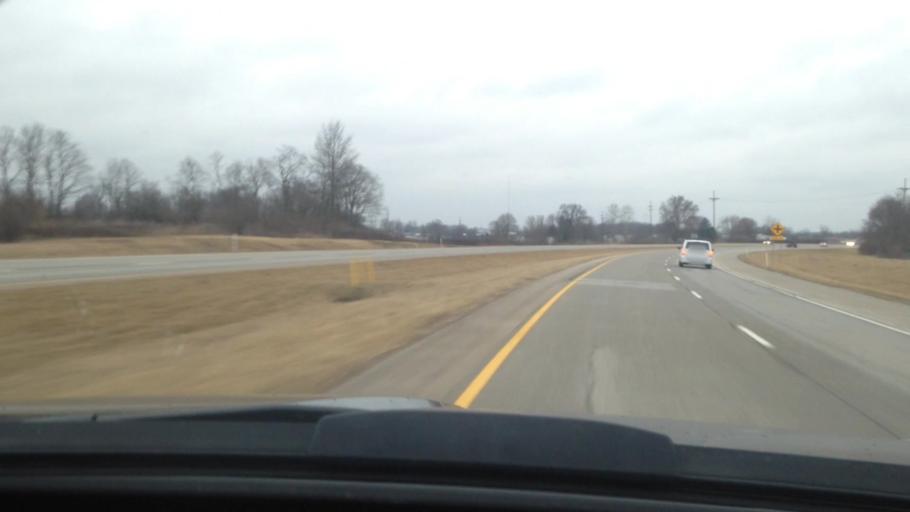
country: US
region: Indiana
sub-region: Delaware County
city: Muncie
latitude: 40.1544
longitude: -85.3544
